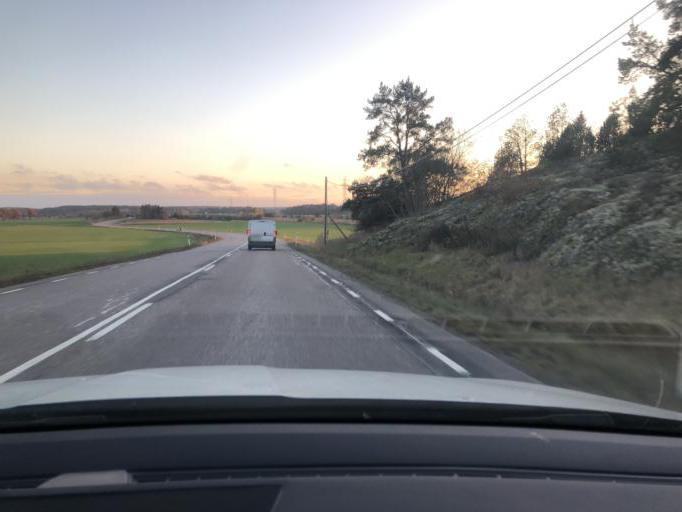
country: SE
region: Soedermanland
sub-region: Strangnas Kommun
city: Akers Styckebruk
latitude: 59.2892
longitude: 17.1084
